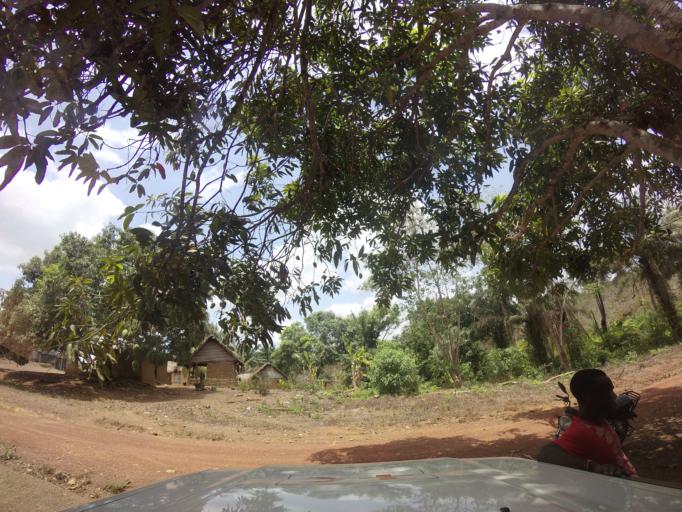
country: SL
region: Southern Province
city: Zimmi
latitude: 7.2083
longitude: -11.2050
